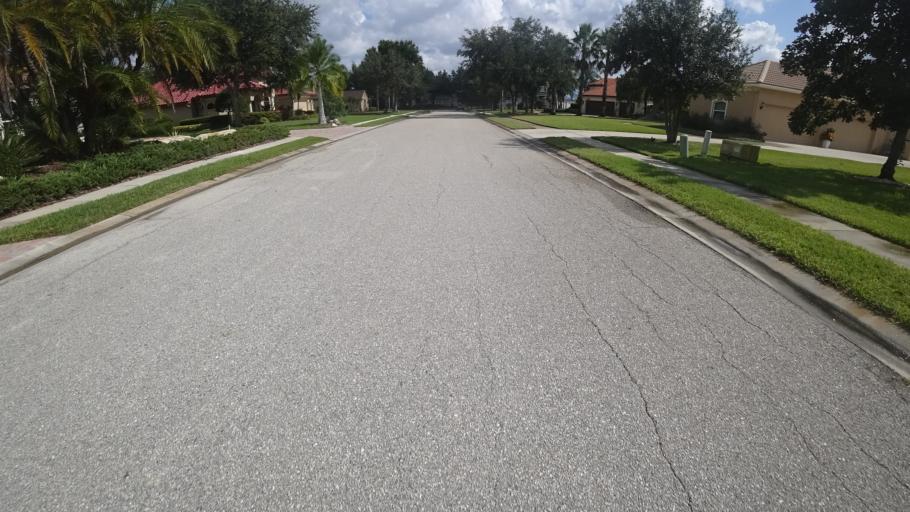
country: US
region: Florida
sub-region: Sarasota County
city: The Meadows
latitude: 27.4086
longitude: -82.4333
